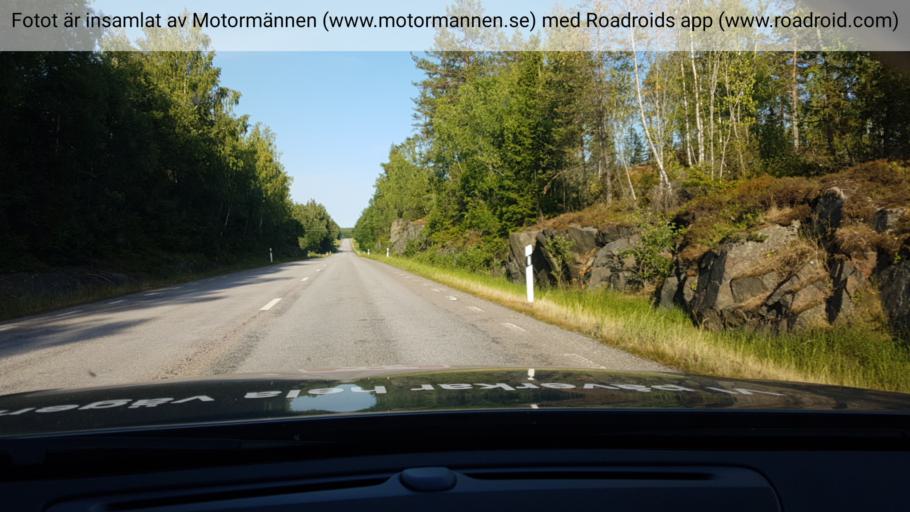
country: SE
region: Uppsala
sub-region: Osthammars Kommun
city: Gimo
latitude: 60.1651
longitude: 18.1698
